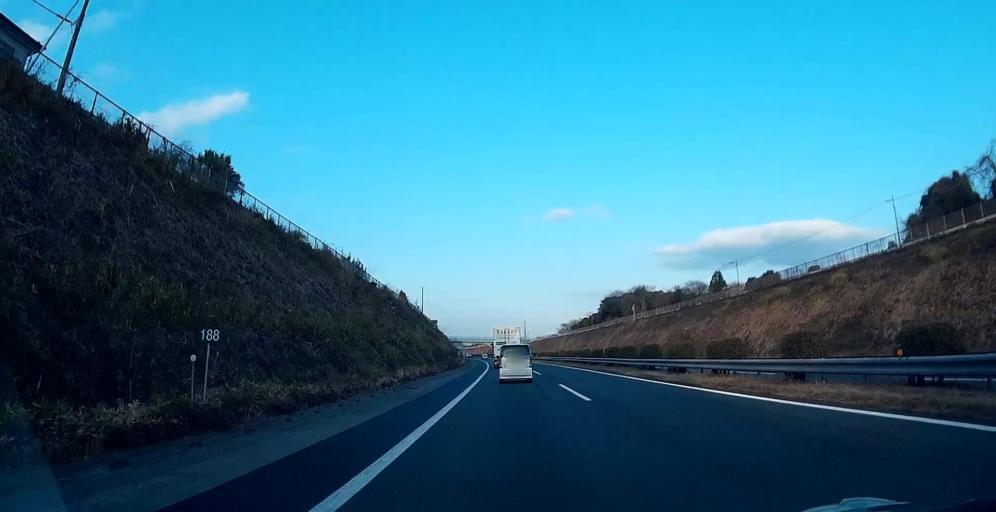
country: JP
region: Kumamoto
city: Uto
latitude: 32.6992
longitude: 130.7495
